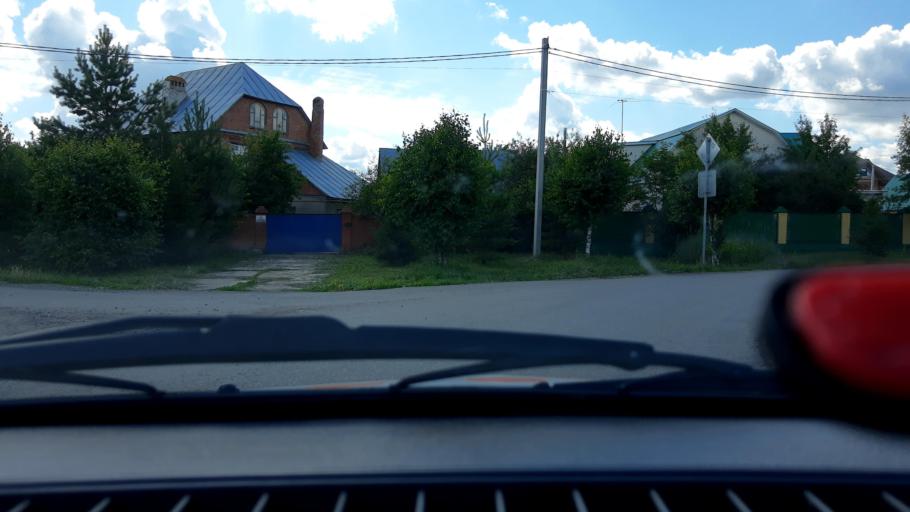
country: RU
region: Bashkortostan
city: Avdon
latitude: 54.4945
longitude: 55.8988
